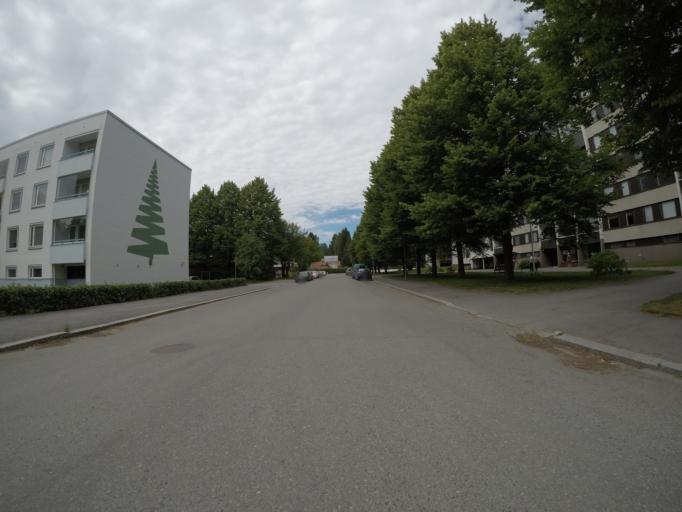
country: FI
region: Haeme
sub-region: Haemeenlinna
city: Haemeenlinna
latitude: 61.0067
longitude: 24.4440
